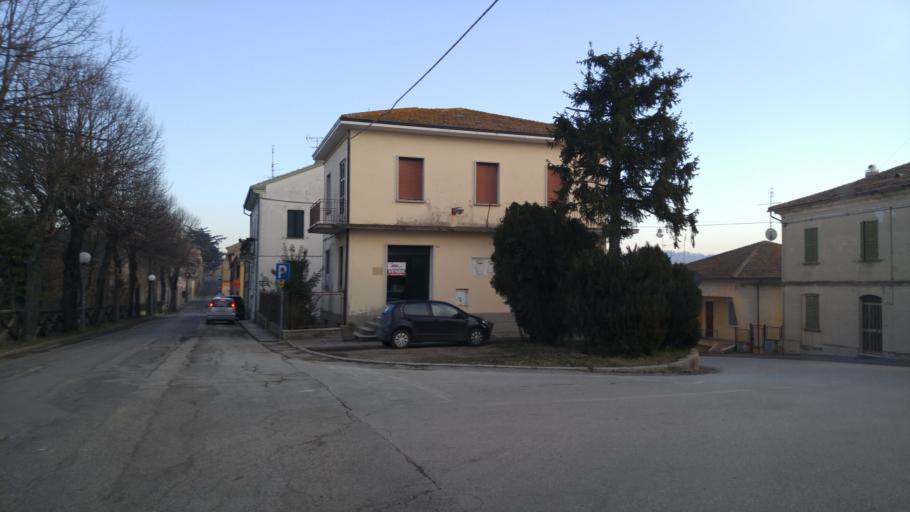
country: IT
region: The Marches
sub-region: Provincia di Pesaro e Urbino
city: Monte Porzio
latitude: 43.6921
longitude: 13.0431
